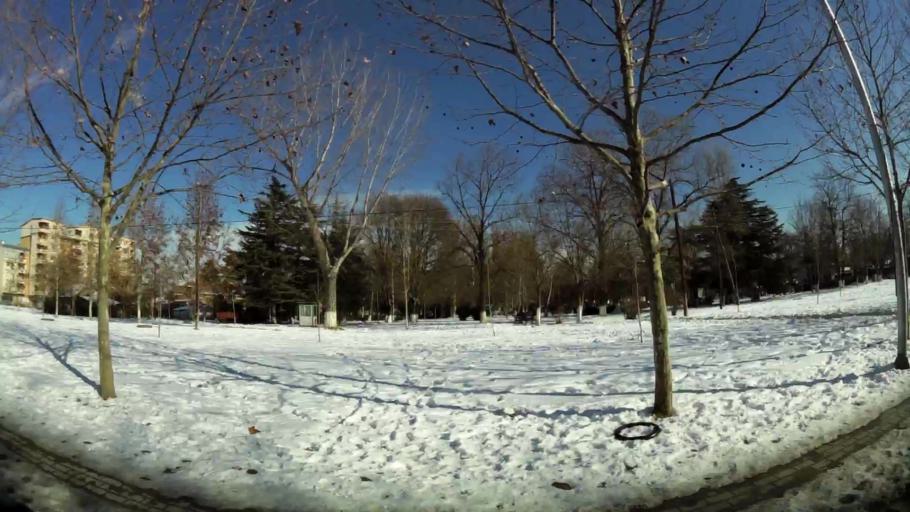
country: MK
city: Krushopek
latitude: 42.0076
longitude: 21.3622
